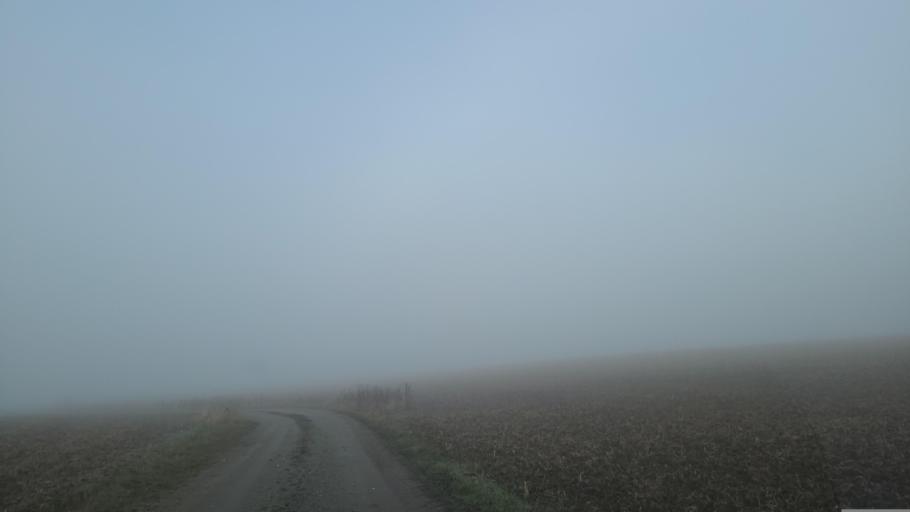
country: SE
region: Uppsala
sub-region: Enkopings Kommun
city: Grillby
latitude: 59.6020
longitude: 17.1746
